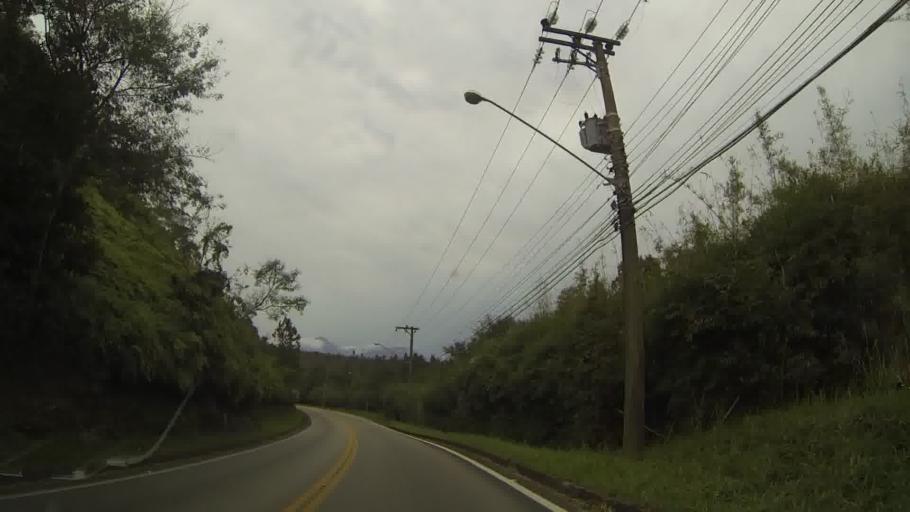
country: BR
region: Sao Paulo
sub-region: Sao Sebastiao
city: Sao Sebastiao
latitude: -23.8271
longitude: -45.5184
